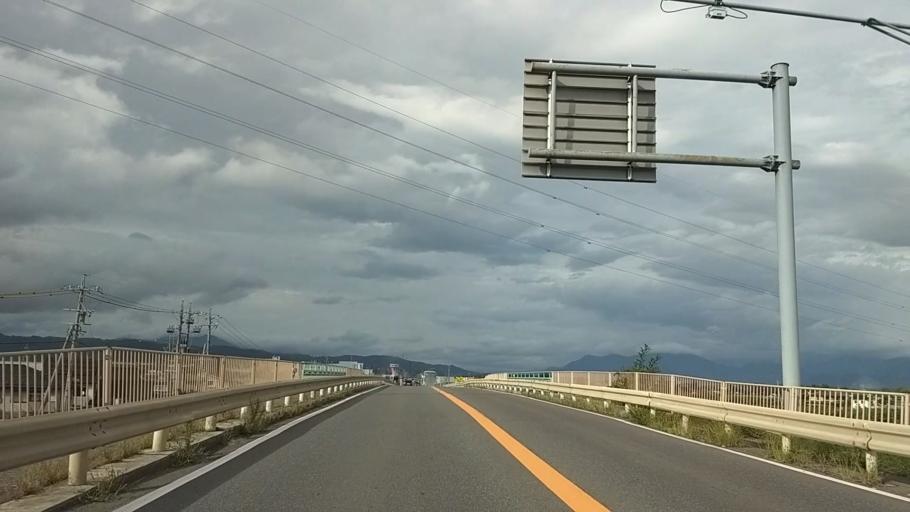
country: JP
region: Nagano
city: Suzaka
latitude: 36.6639
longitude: 138.2622
